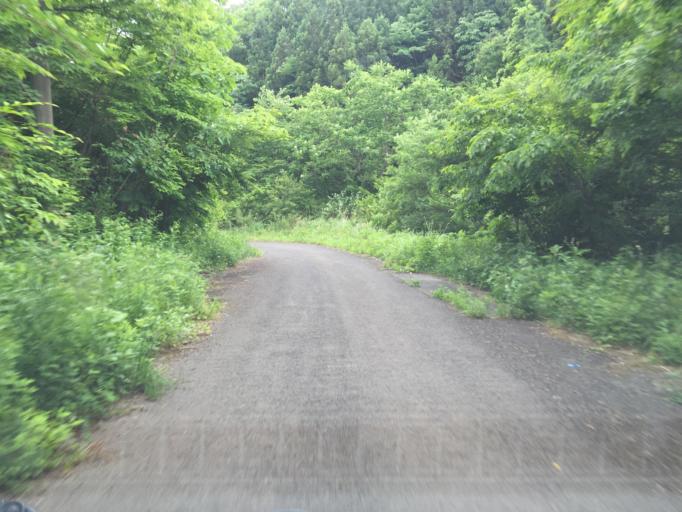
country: JP
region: Fukushima
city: Fukushima-shi
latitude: 37.7154
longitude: 140.3339
